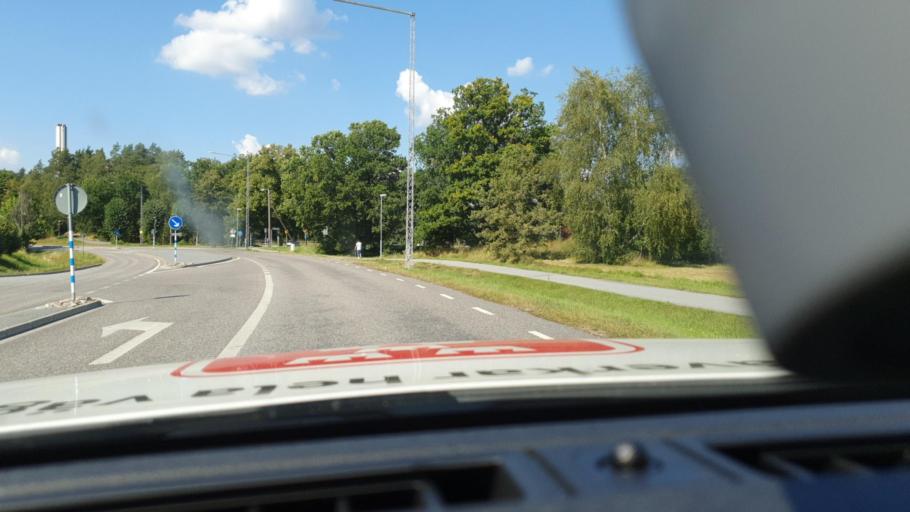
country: SE
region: Stockholm
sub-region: Jarfalla Kommun
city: Jakobsberg
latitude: 59.4248
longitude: 17.8546
